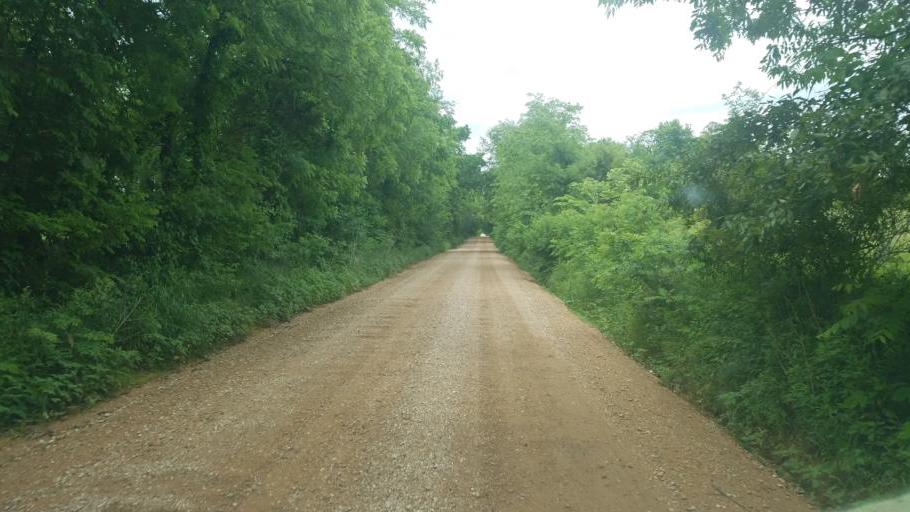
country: US
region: Missouri
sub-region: Moniteau County
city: California
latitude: 38.6228
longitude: -92.6191
